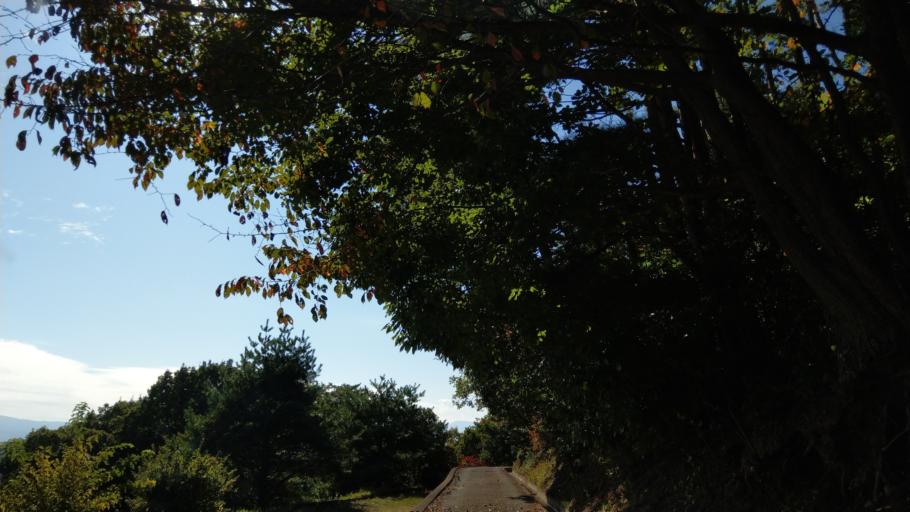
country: JP
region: Nagano
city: Komoro
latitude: 36.3393
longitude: 138.4380
